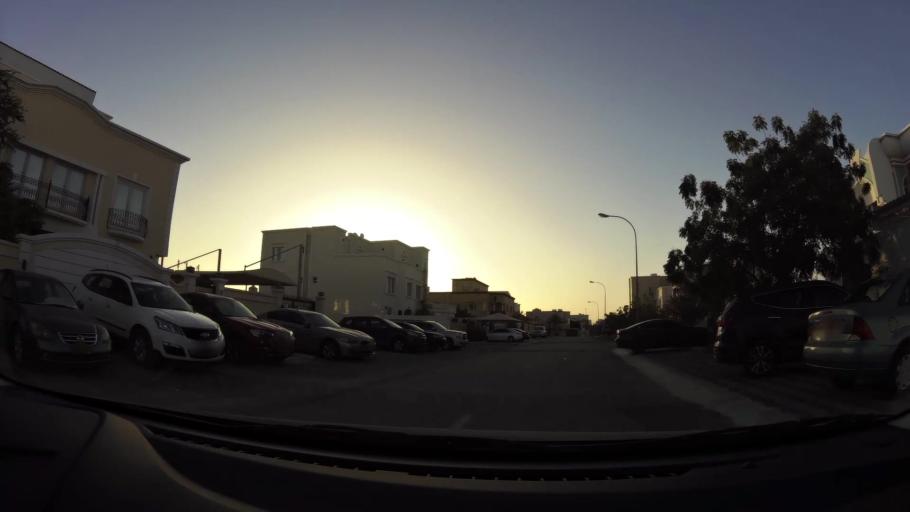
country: OM
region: Muhafazat Masqat
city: As Sib al Jadidah
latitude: 23.6055
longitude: 58.2291
